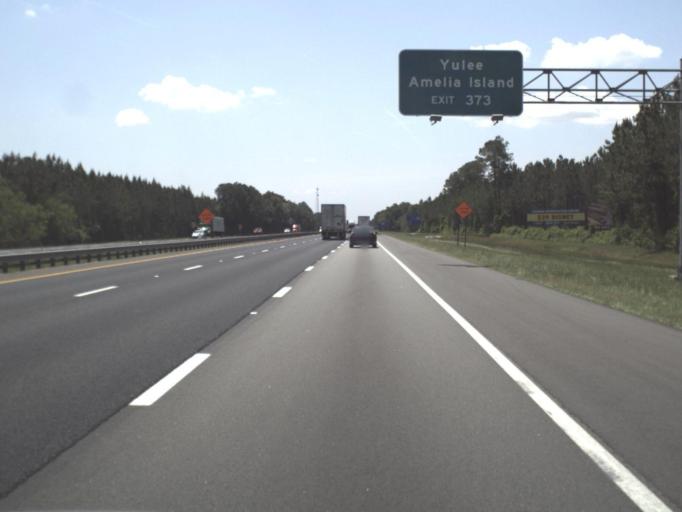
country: US
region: Florida
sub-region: Nassau County
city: Yulee
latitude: 30.6340
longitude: -81.6553
